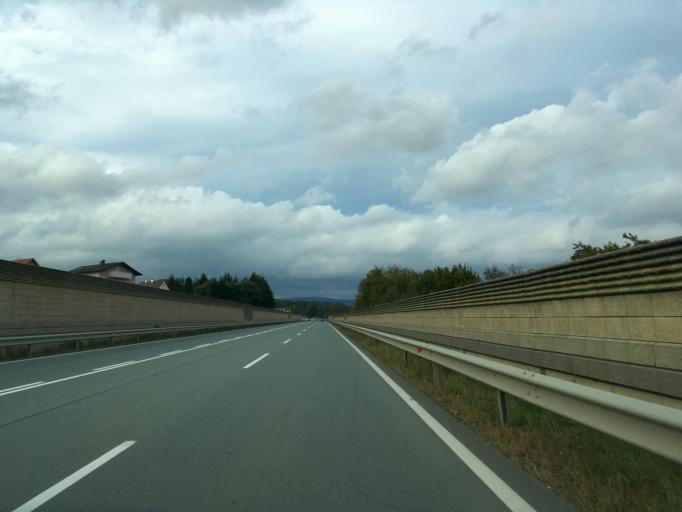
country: AT
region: Styria
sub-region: Politischer Bezirk Hartberg-Fuerstenfeld
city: Rohrbach an der Lafnitz
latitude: 47.3947
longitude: 16.0013
